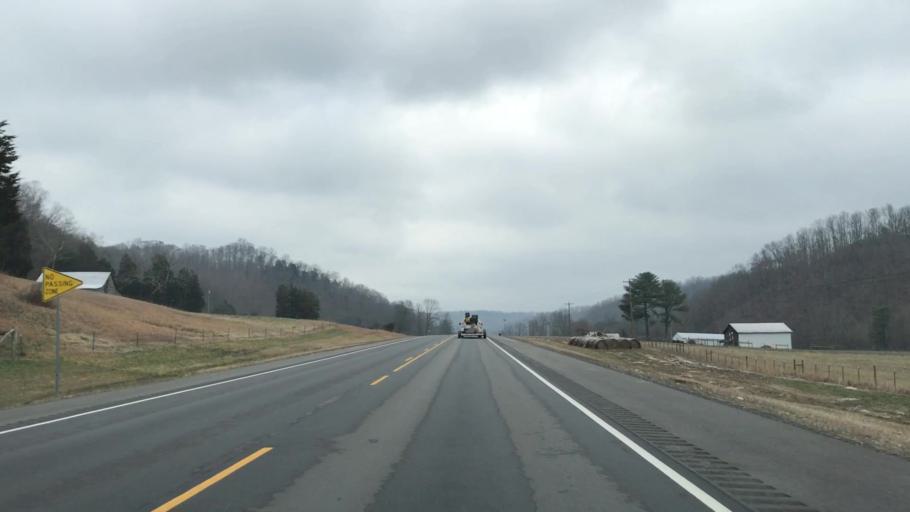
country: US
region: Kentucky
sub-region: Cumberland County
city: Burkesville
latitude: 36.8795
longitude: -85.4014
